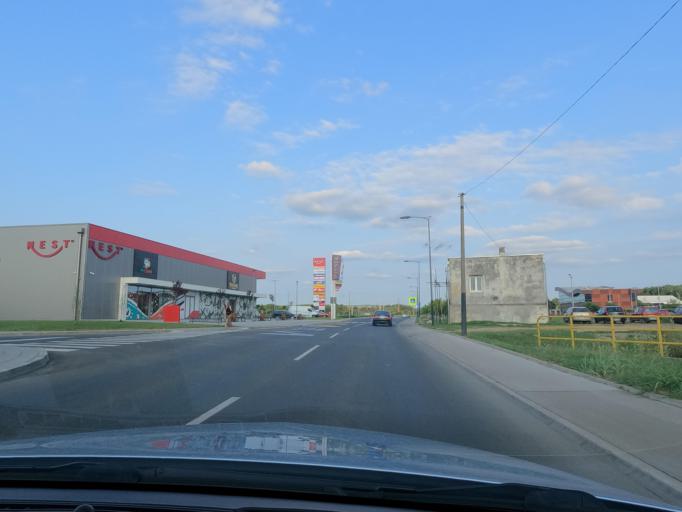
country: RS
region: Central Serbia
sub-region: Belgrade
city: Obrenovac
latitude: 44.6580
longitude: 20.2125
